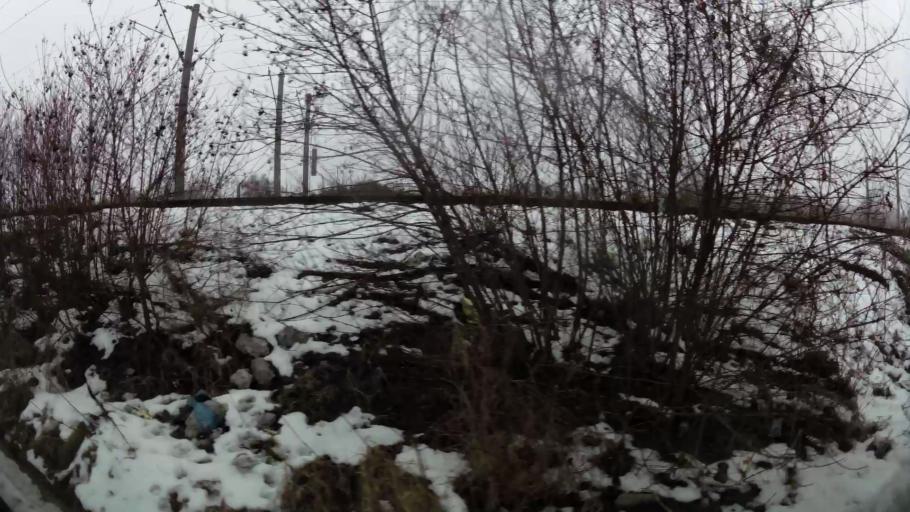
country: RO
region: Ilfov
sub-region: Comuna Chitila
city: Rudeni
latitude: 44.4690
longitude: 25.9784
